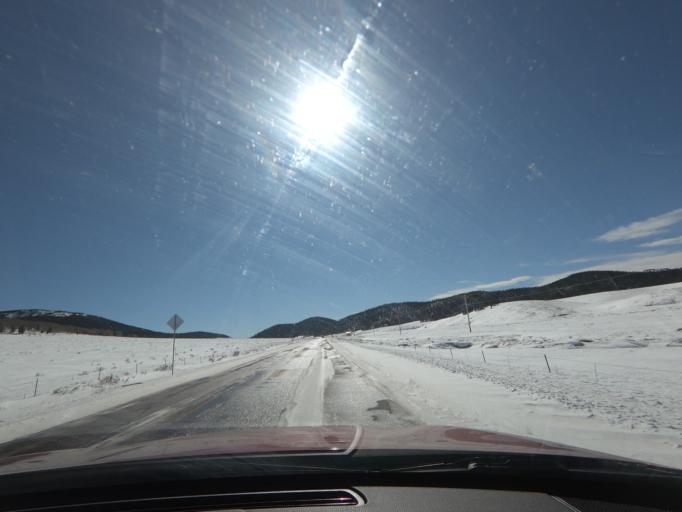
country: US
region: Colorado
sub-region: Teller County
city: Cripple Creek
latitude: 38.7713
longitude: -105.1200
